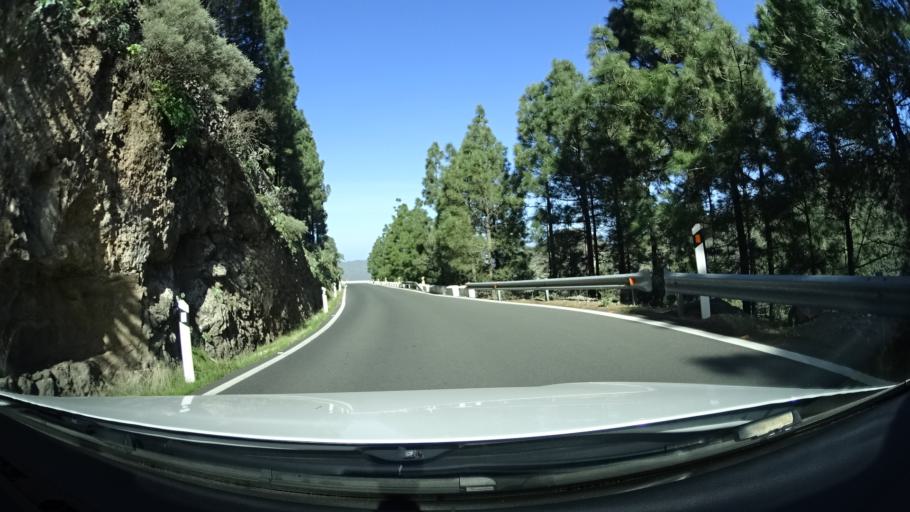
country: ES
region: Canary Islands
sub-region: Provincia de Las Palmas
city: Artenara
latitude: 28.0240
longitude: -15.6259
